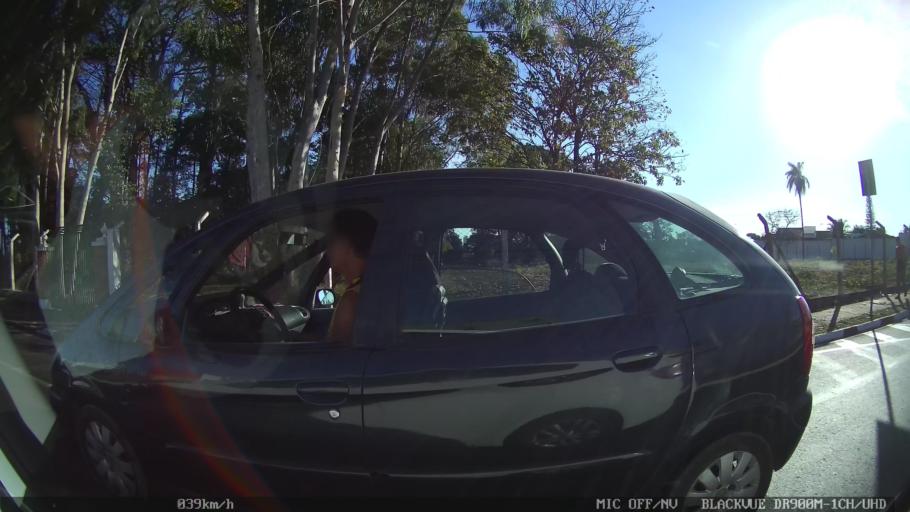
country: BR
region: Sao Paulo
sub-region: Franca
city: Franca
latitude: -20.5197
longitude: -47.3710
